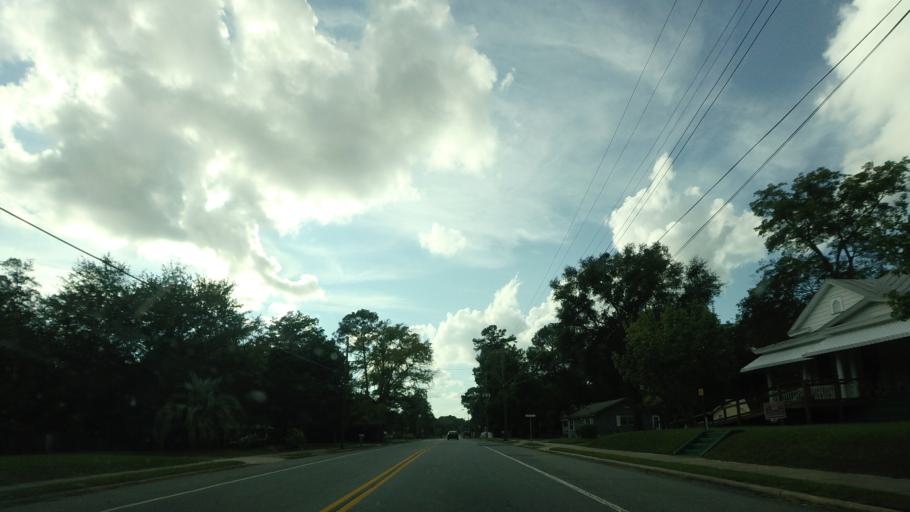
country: US
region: Georgia
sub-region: Pulaski County
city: Hawkinsville
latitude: 32.2843
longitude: -83.4751
